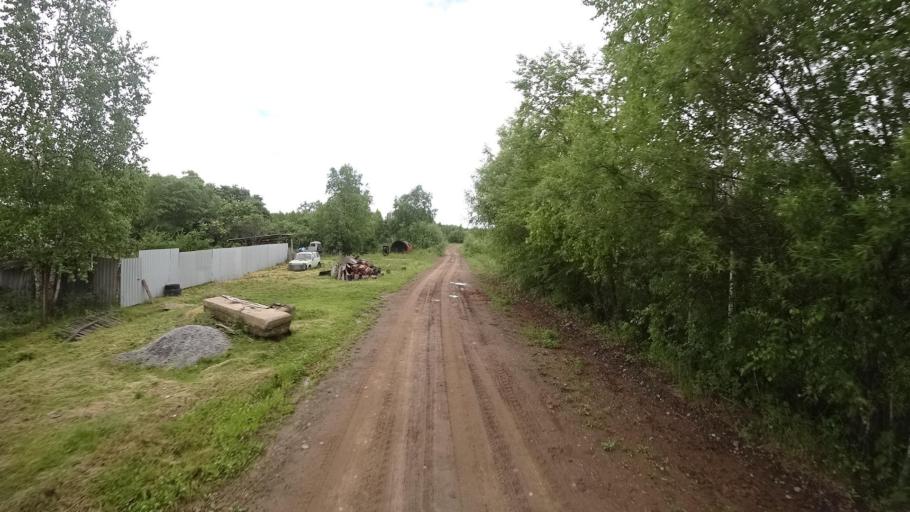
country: RU
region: Khabarovsk Krai
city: Amursk
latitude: 49.9163
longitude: 136.1625
